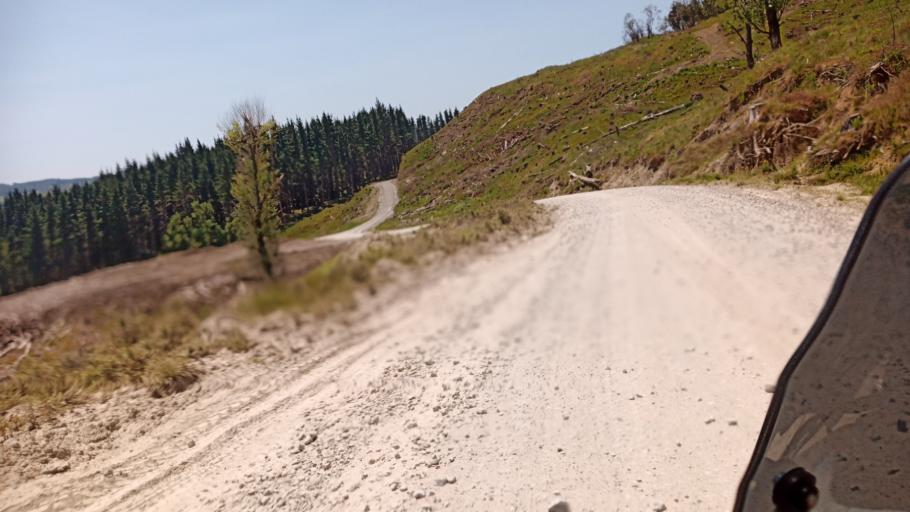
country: NZ
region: Gisborne
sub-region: Gisborne District
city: Gisborne
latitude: -38.2883
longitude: 178.0083
